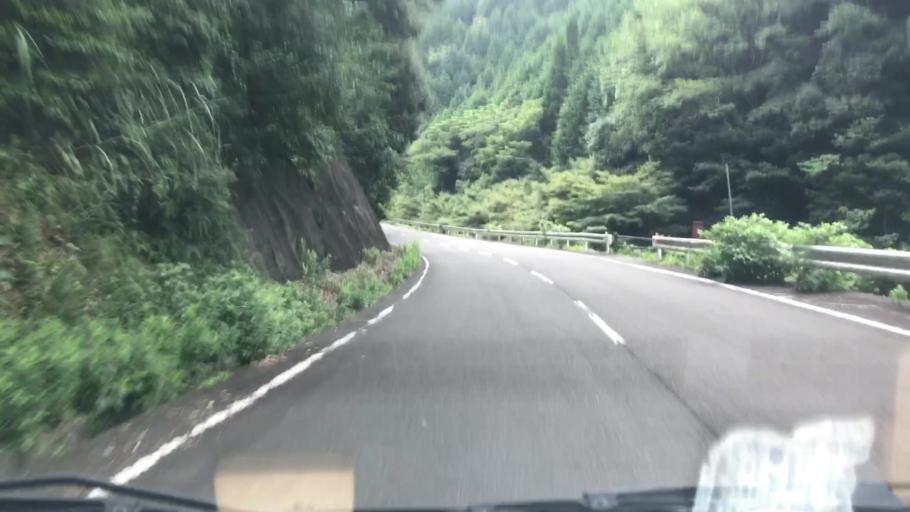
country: JP
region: Saga Prefecture
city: Takeocho-takeo
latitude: 33.2271
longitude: 130.0039
